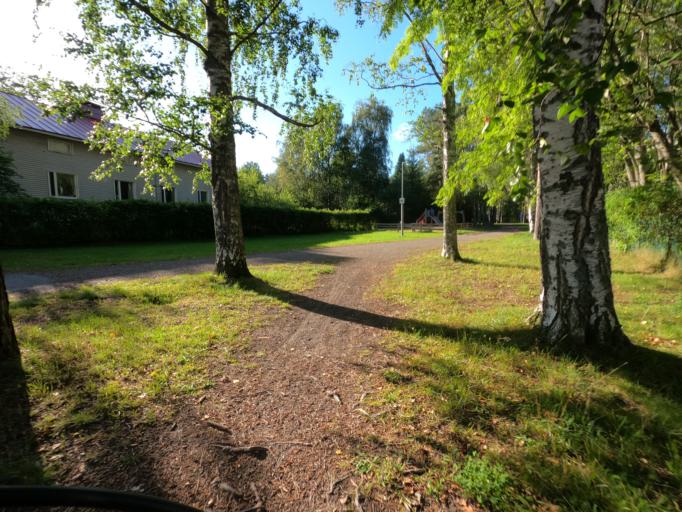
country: FI
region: North Karelia
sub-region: Joensuu
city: Joensuu
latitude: 62.6097
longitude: 29.7492
